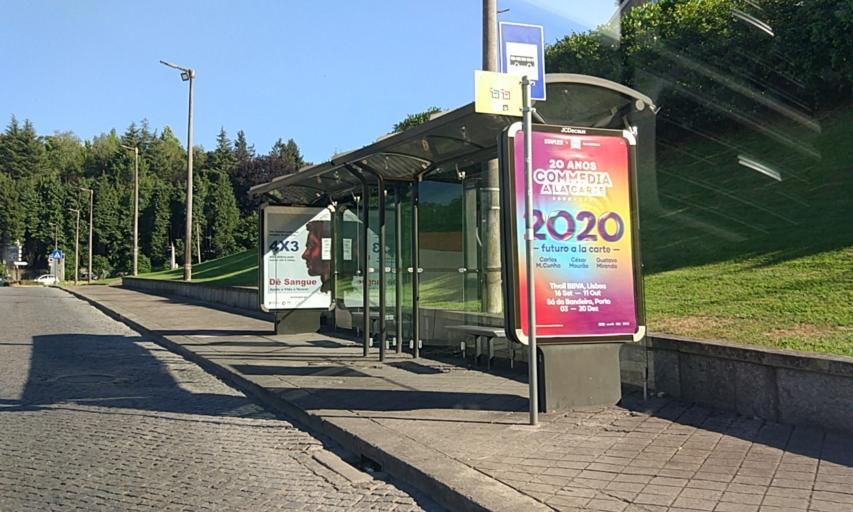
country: PT
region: Porto
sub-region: Santo Tirso
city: Santo Tirso
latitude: 41.3420
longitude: -8.4727
